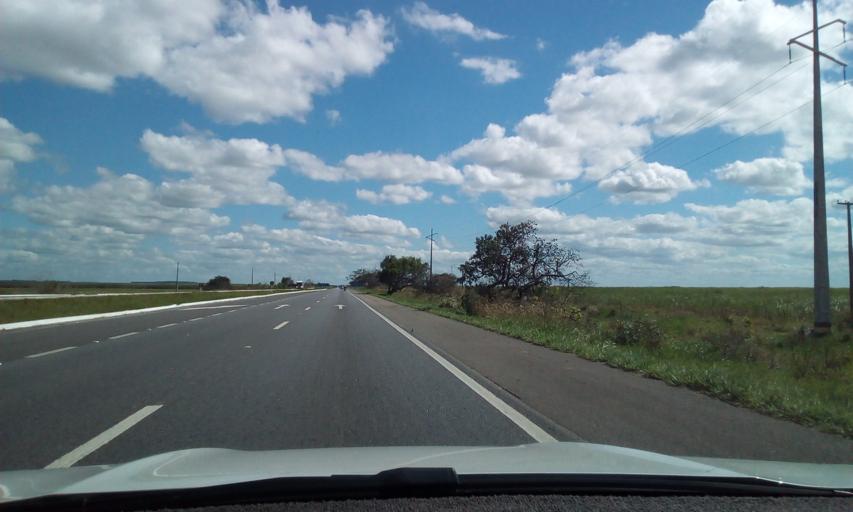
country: BR
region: Paraiba
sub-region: Cruz Do Espirito Santo
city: Cruz do Espirito Santo
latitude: -7.1810
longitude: -35.0493
